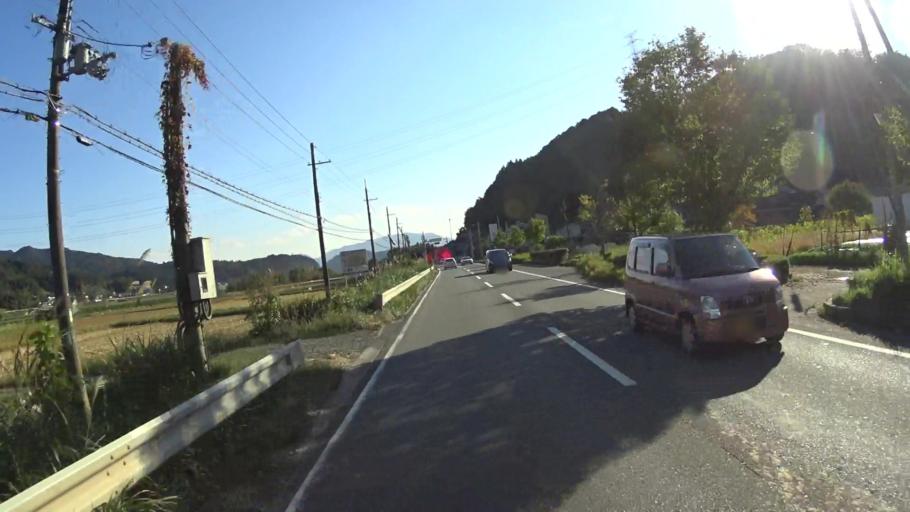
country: JP
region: Kyoto
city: Fukuchiyama
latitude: 35.3590
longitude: 135.1135
